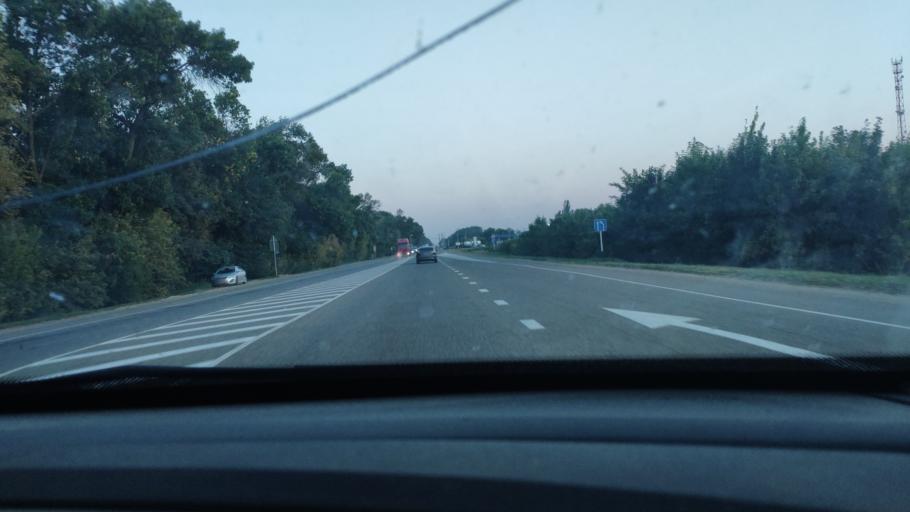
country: RU
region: Krasnodarskiy
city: Medvedovskaya
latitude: 45.4515
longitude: 38.9910
